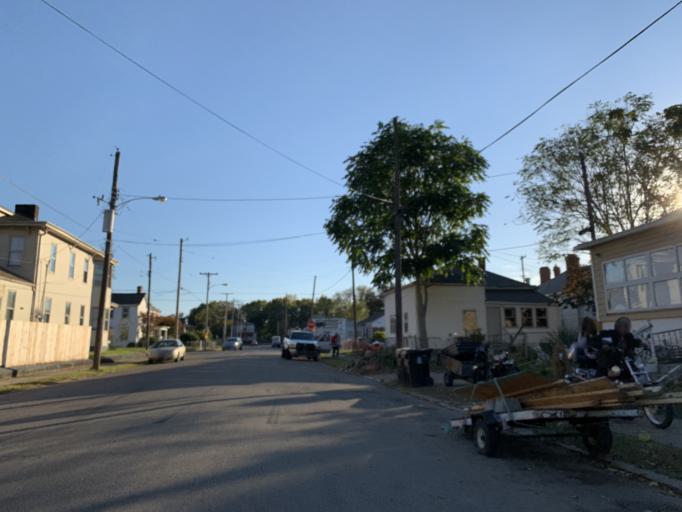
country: US
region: Indiana
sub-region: Floyd County
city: New Albany
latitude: 38.2746
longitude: -85.7939
